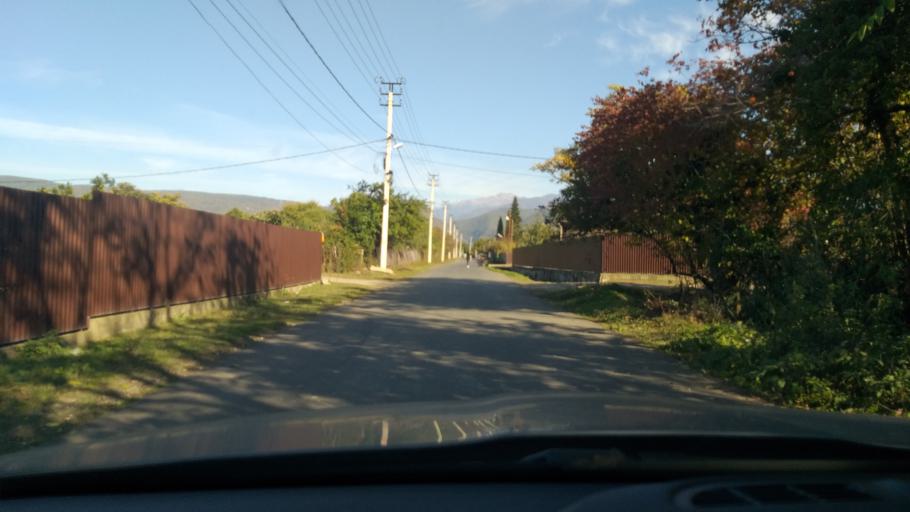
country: GE
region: Abkhazia
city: Sokhumi
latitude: 43.0161
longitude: 40.9645
